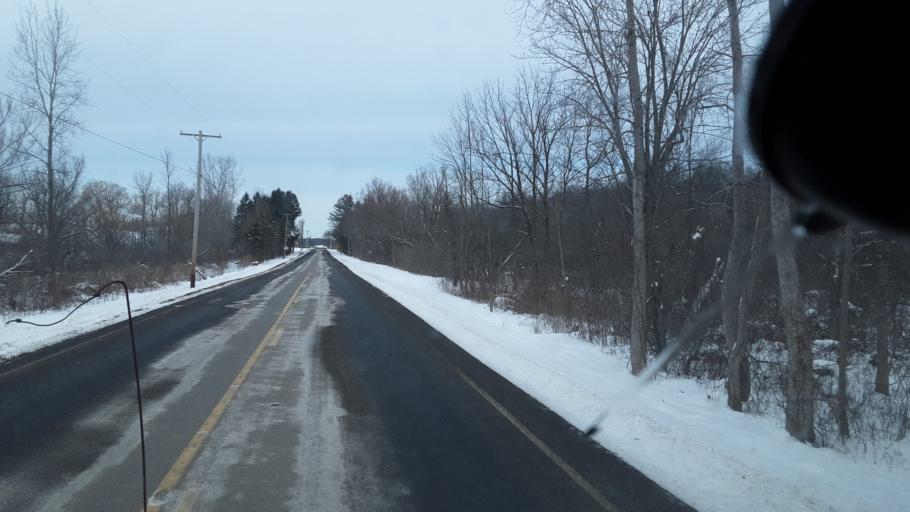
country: US
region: New York
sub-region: Wayne County
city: Lyons
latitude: 43.1007
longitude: -77.0439
